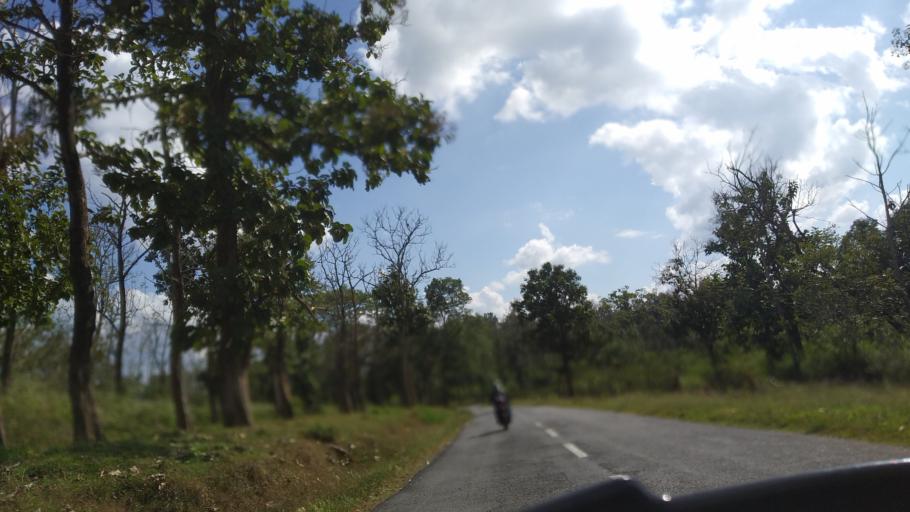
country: IN
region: Kerala
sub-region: Wayanad
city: Panamaram
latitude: 11.9208
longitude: 76.0664
